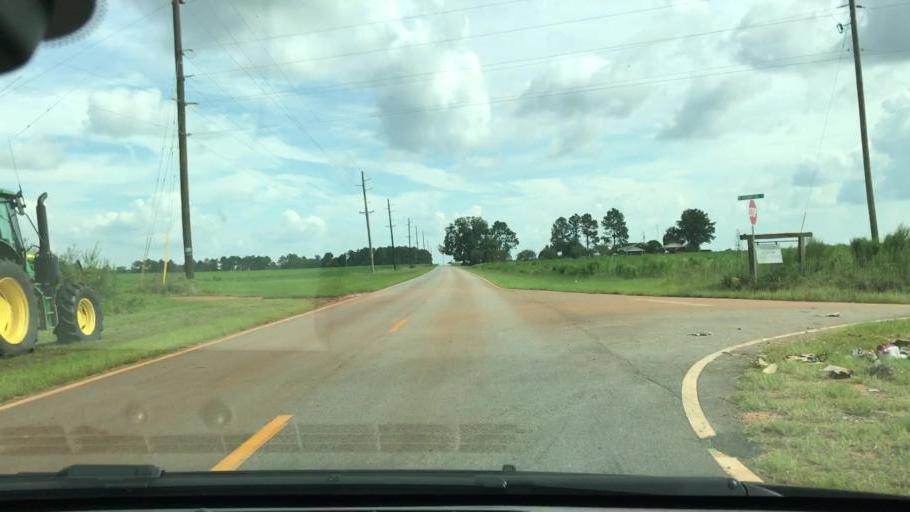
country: US
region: Georgia
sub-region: Clay County
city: Fort Gaines
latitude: 31.5398
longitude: -84.9619
